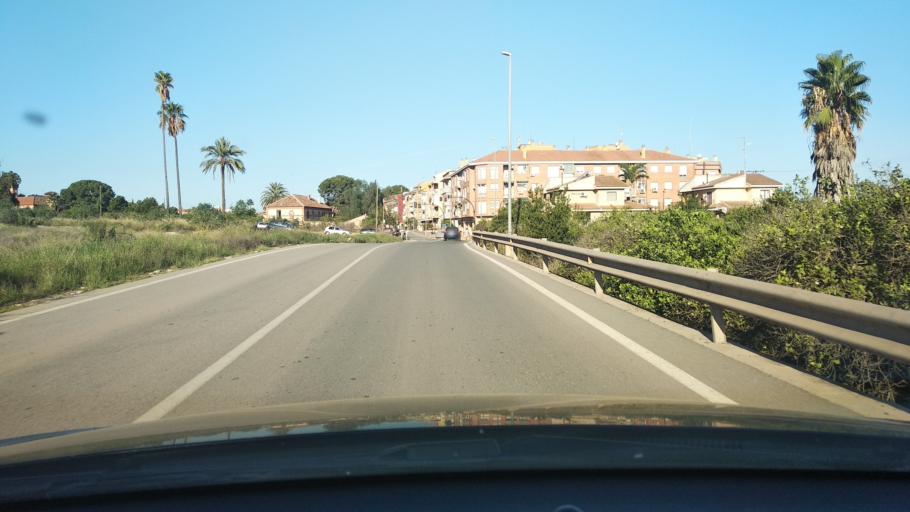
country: ES
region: Murcia
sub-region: Murcia
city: Murcia
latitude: 37.9443
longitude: -1.1223
